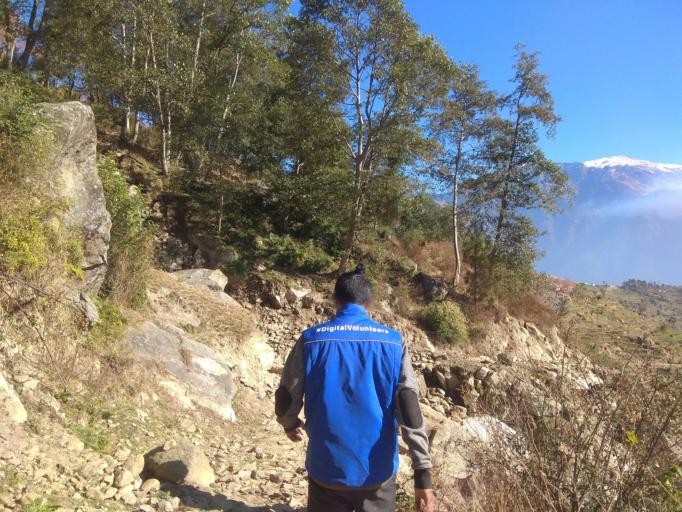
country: NP
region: Far Western
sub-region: Seti Zone
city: Achham
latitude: 29.2590
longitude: 81.6326
